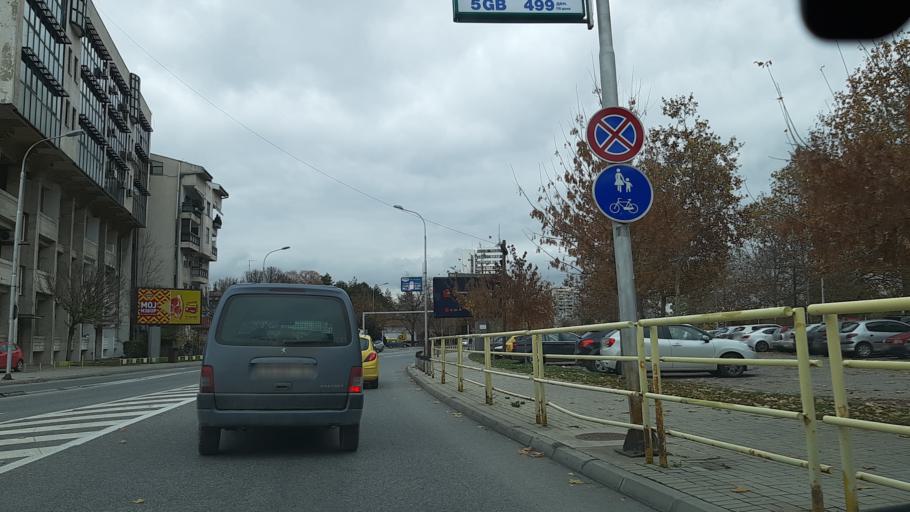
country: MK
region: Karpos
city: Skopje
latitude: 41.9942
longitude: 21.4191
